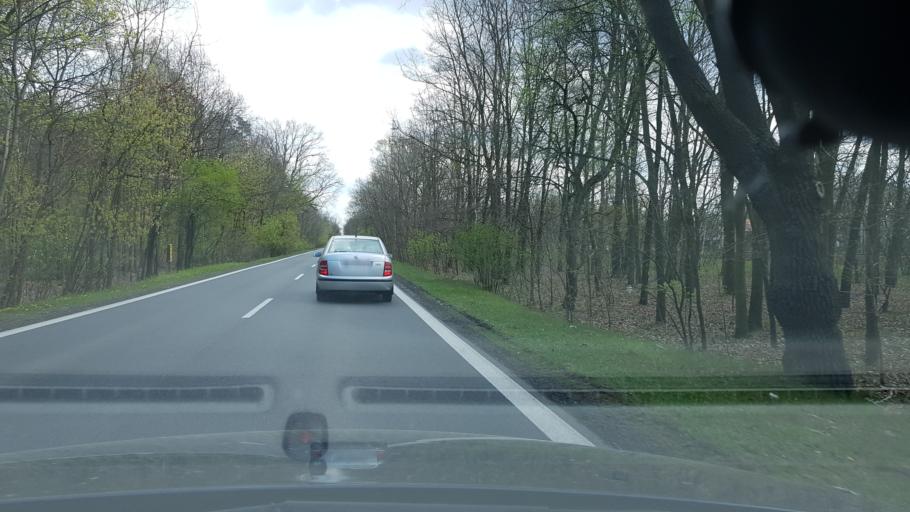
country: PL
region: Masovian Voivodeship
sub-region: Warszawa
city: Wesola
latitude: 52.2536
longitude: 21.2423
